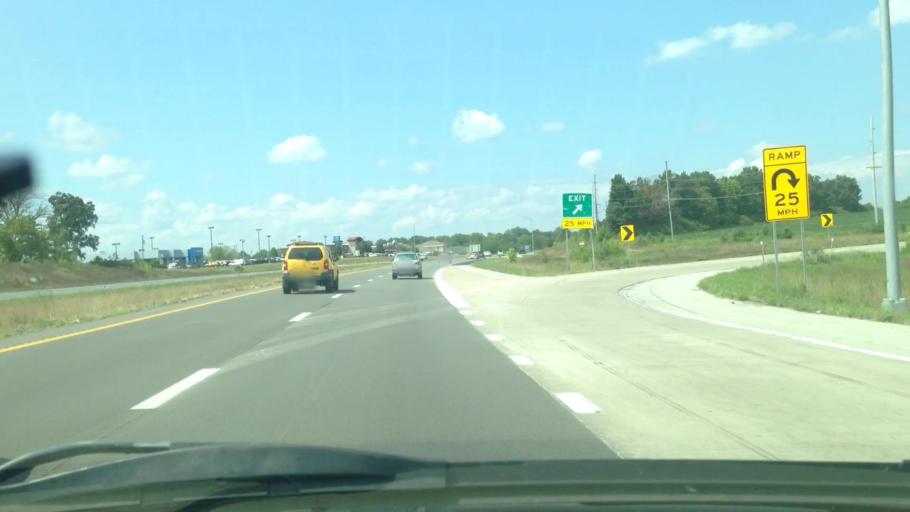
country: US
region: Missouri
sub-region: Lincoln County
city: Troy
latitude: 38.9672
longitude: -90.9570
